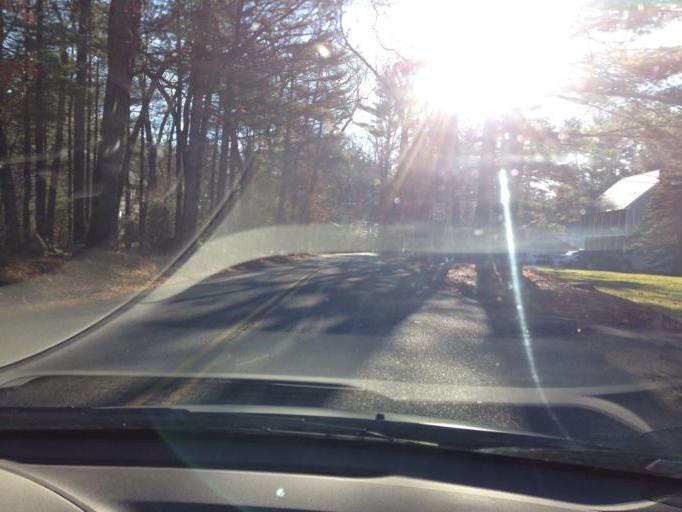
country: US
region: Massachusetts
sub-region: Middlesex County
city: Bedford
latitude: 42.5177
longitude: -71.2729
